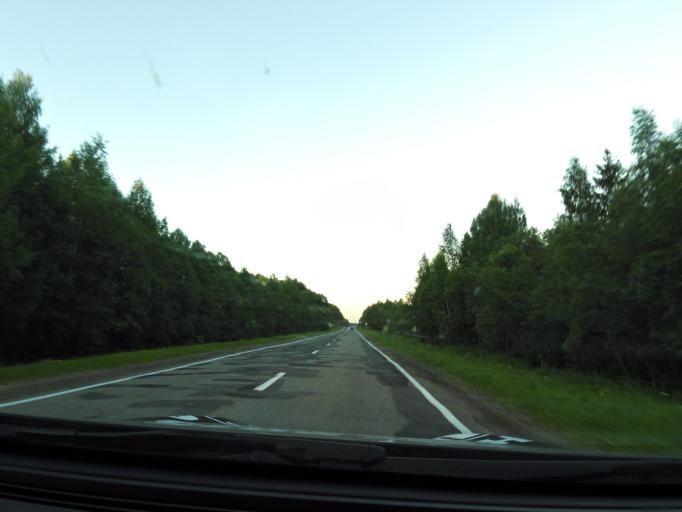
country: RU
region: Jaroslavl
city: Lyubim
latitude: 58.3575
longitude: 40.5801
